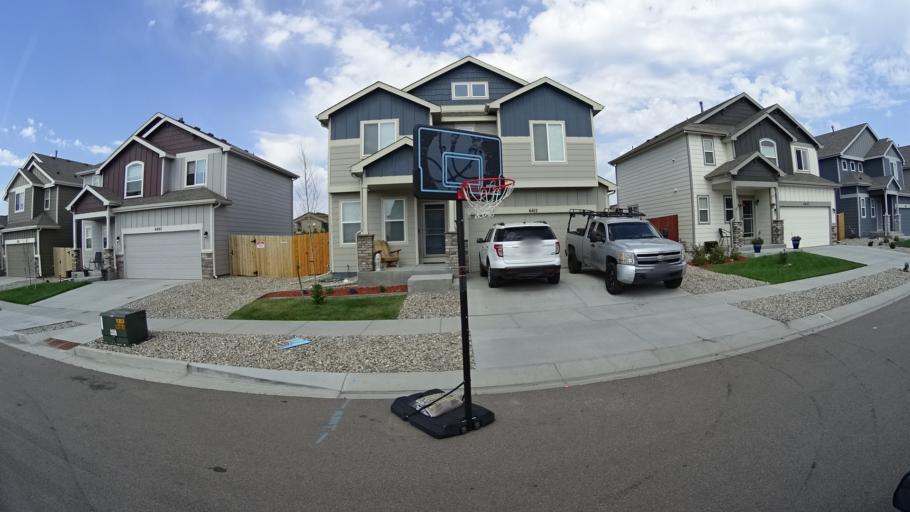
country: US
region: Colorado
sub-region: El Paso County
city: Cimarron Hills
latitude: 38.9237
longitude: -104.6816
